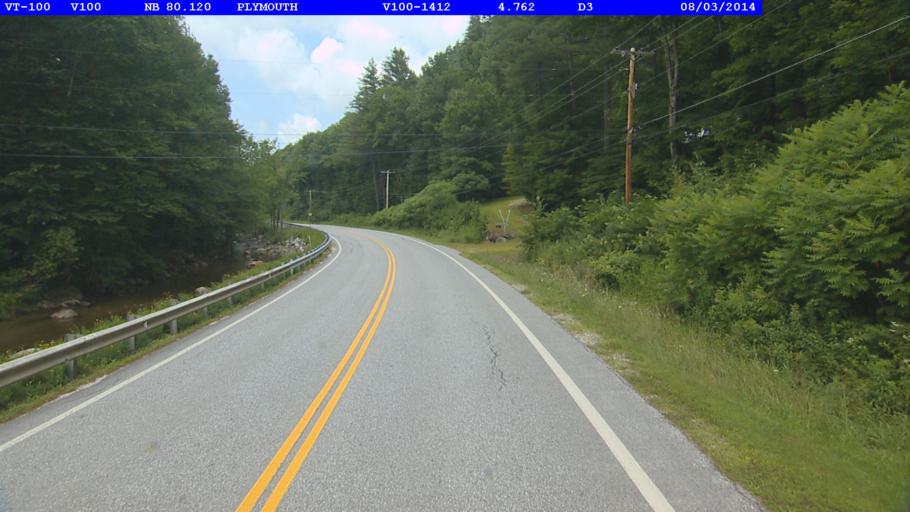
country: US
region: Vermont
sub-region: Windsor County
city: Woodstock
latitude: 43.5232
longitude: -72.7334
